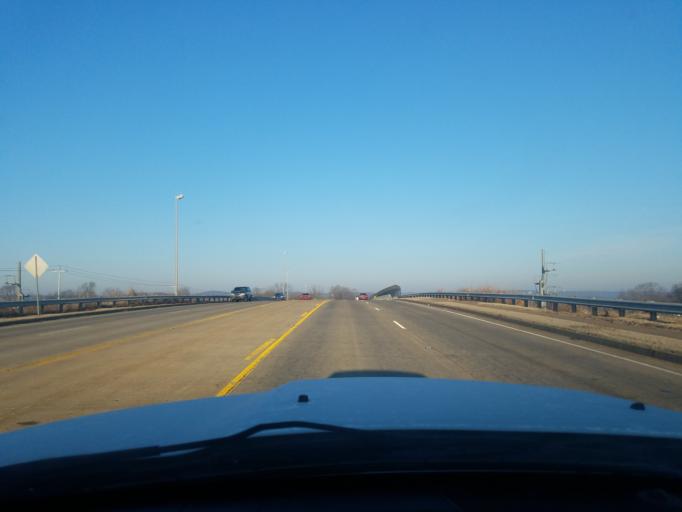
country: US
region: Kentucky
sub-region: Warren County
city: Bowling Green
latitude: 36.9666
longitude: -86.4769
